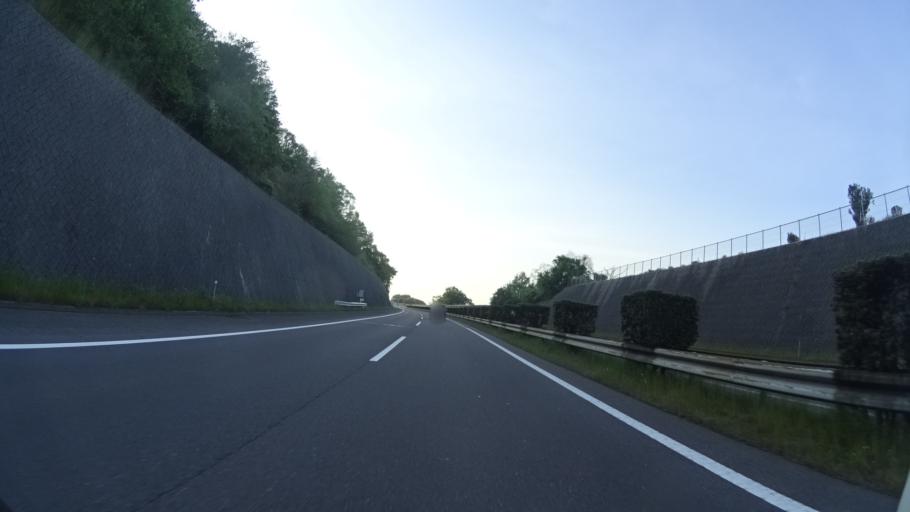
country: JP
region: Kagawa
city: Sakaidecho
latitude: 34.3158
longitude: 133.8385
